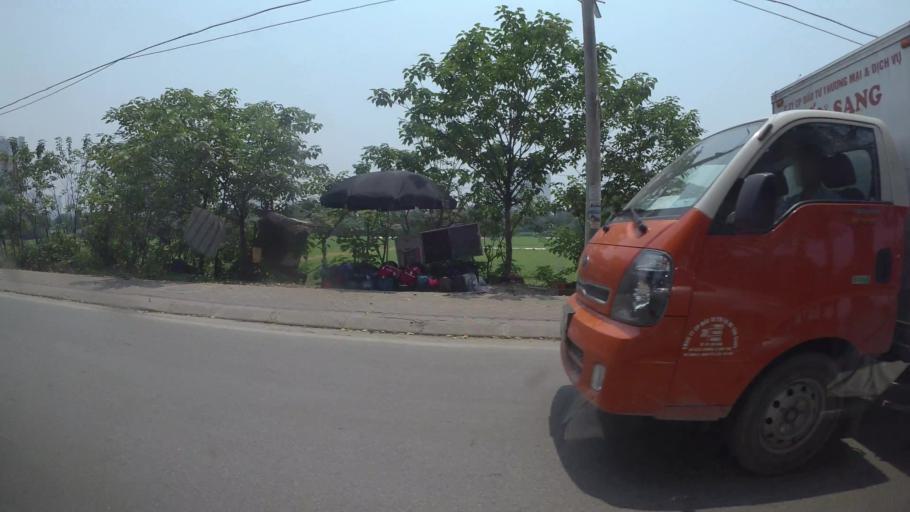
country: VN
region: Ha Noi
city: Thanh Xuan
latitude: 20.9916
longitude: 105.7811
